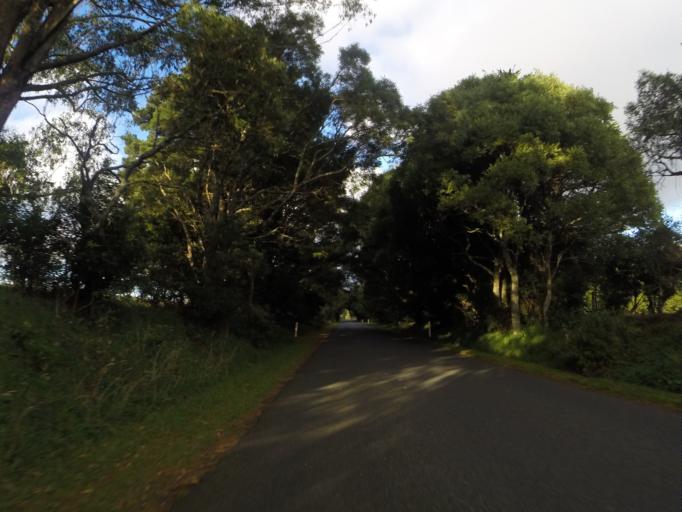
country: AU
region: New South Wales
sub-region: Shoalhaven Shire
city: Kangaroo Valley
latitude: -34.6030
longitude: 150.5475
